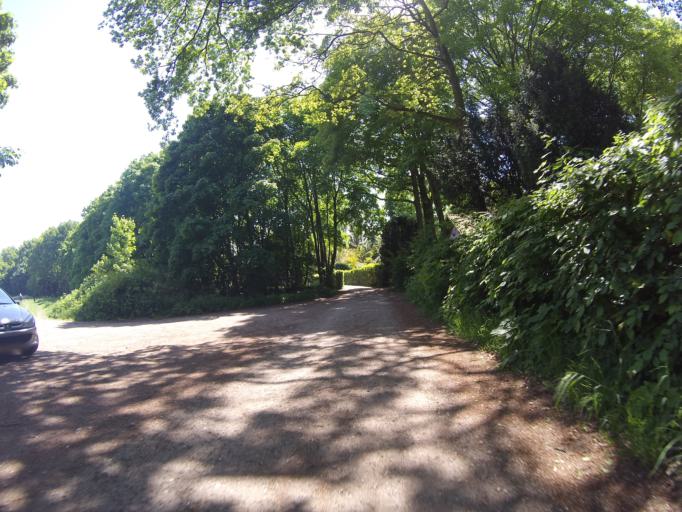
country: NL
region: North Holland
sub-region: Gemeente Hilversum
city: Hilversum
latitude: 52.2371
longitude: 5.1657
